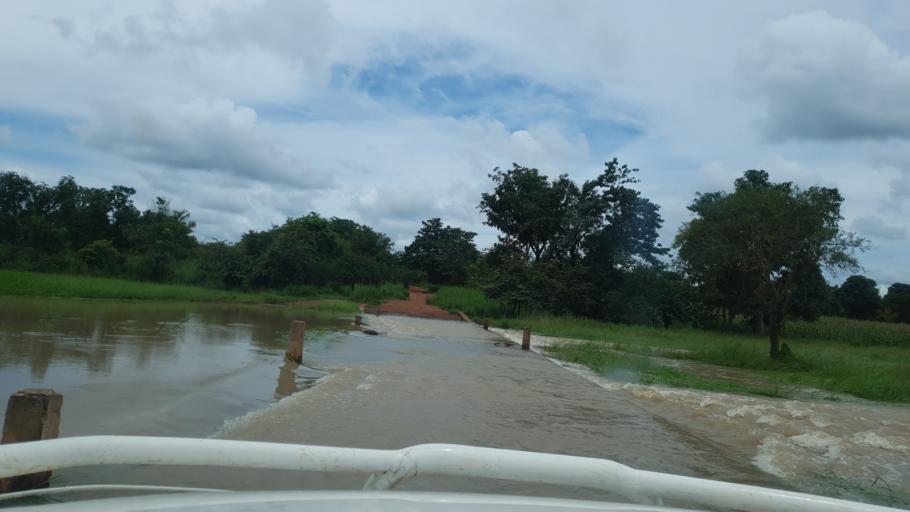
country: CI
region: Savanes
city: Tengrela
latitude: 10.5107
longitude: -6.9246
